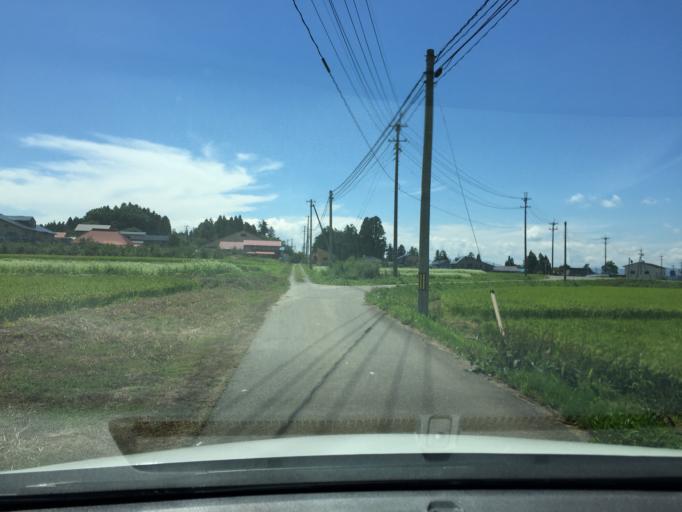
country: JP
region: Fukushima
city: Inawashiro
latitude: 37.5682
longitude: 140.1360
